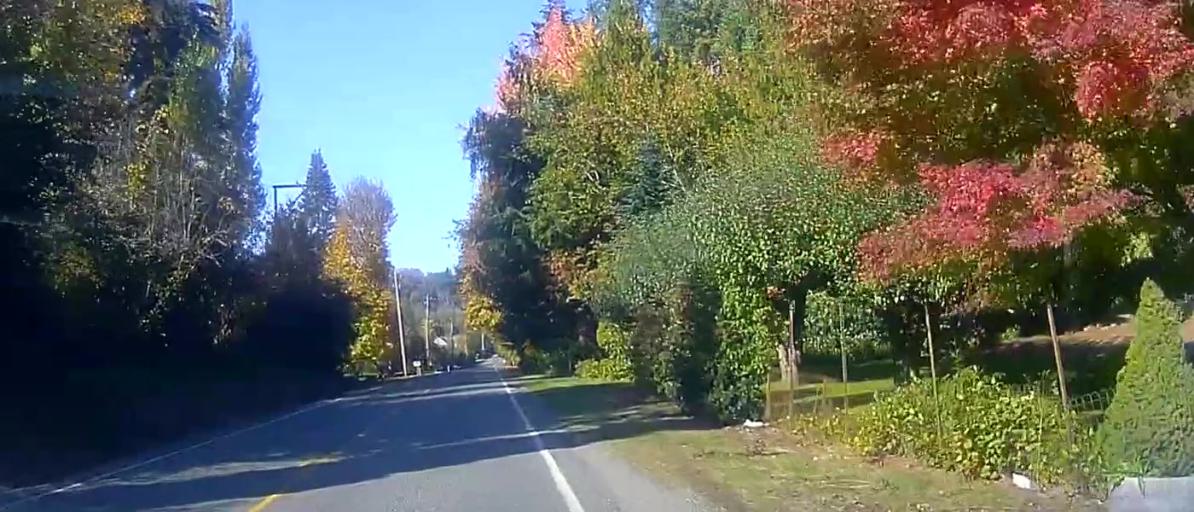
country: US
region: Washington
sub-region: Skagit County
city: Big Lake
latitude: 48.3874
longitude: -122.2436
